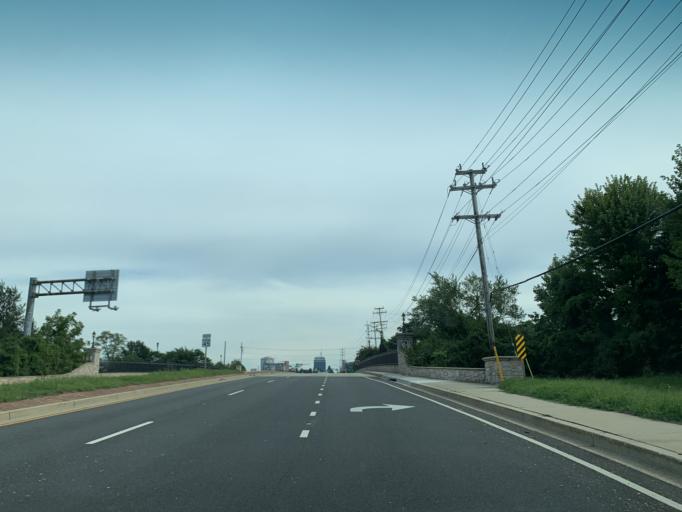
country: US
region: Maryland
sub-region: Baltimore County
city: Lutherville
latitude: 39.4145
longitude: -76.6129
